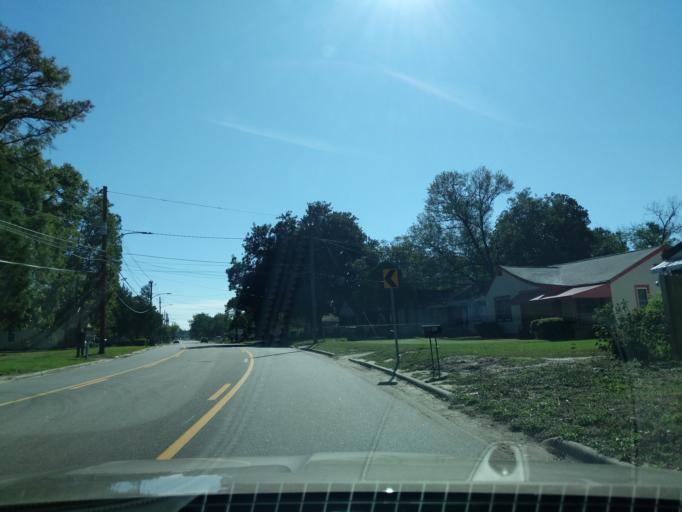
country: US
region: Georgia
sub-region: Richmond County
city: Augusta
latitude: 33.4435
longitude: -82.0045
